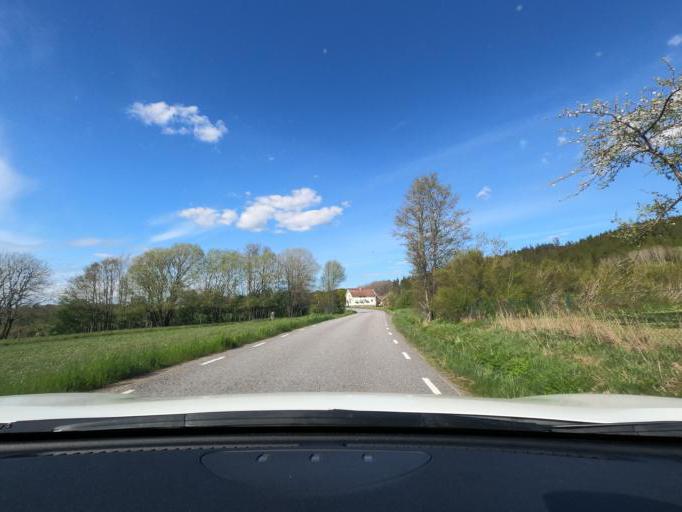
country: SE
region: Vaestra Goetaland
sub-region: Harryda Kommun
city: Ravlanda
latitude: 57.6191
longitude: 12.4958
